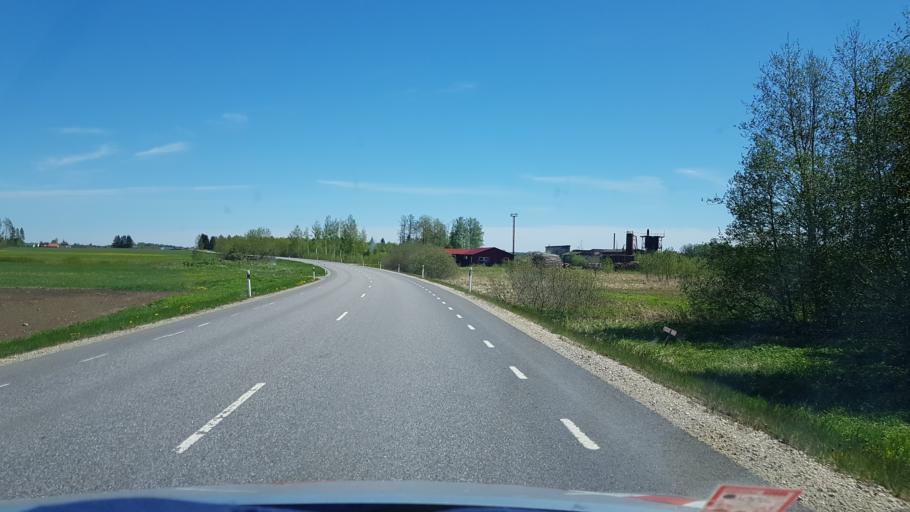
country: EE
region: Tartu
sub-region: UElenurme vald
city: Ulenurme
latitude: 58.3103
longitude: 26.6735
